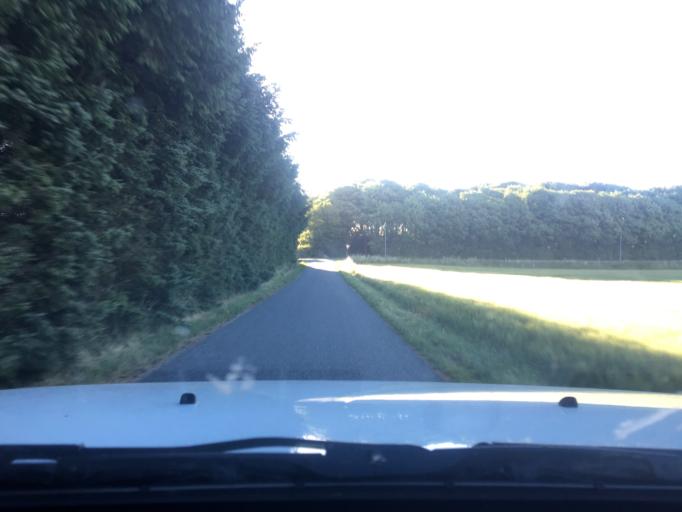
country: DK
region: Central Jutland
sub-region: Randers Kommune
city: Randers
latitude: 56.4010
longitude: 10.0664
